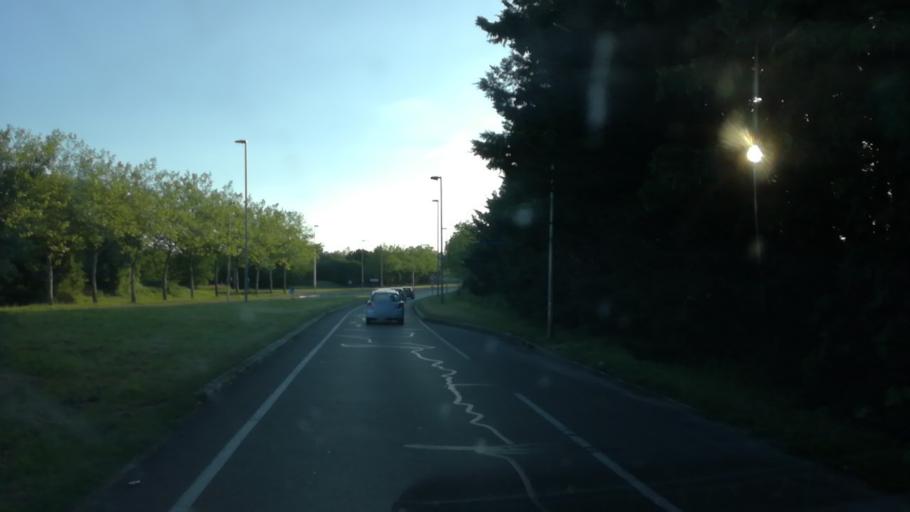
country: FR
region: Ile-de-France
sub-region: Departement des Yvelines
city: Elancourt
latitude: 48.7776
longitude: 1.9672
